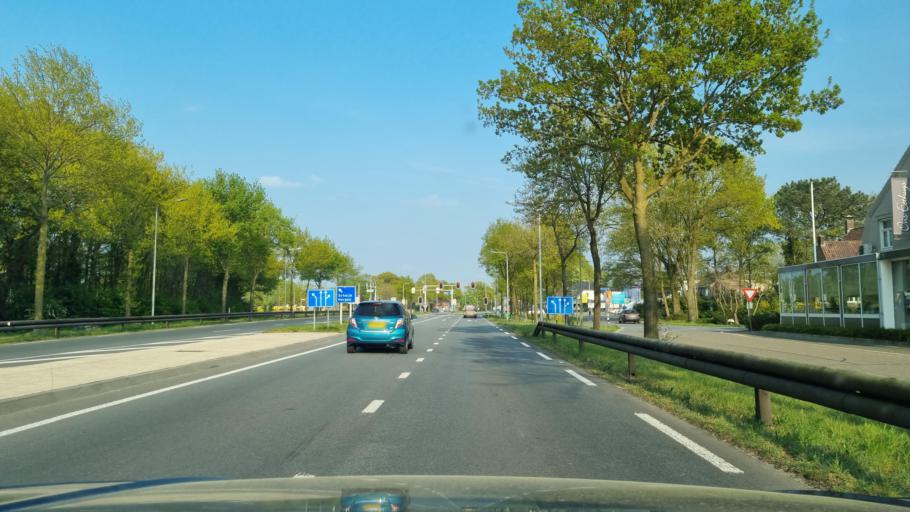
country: NL
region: North Brabant
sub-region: Gemeente Landerd
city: Schaijk
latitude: 51.7372
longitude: 5.6327
